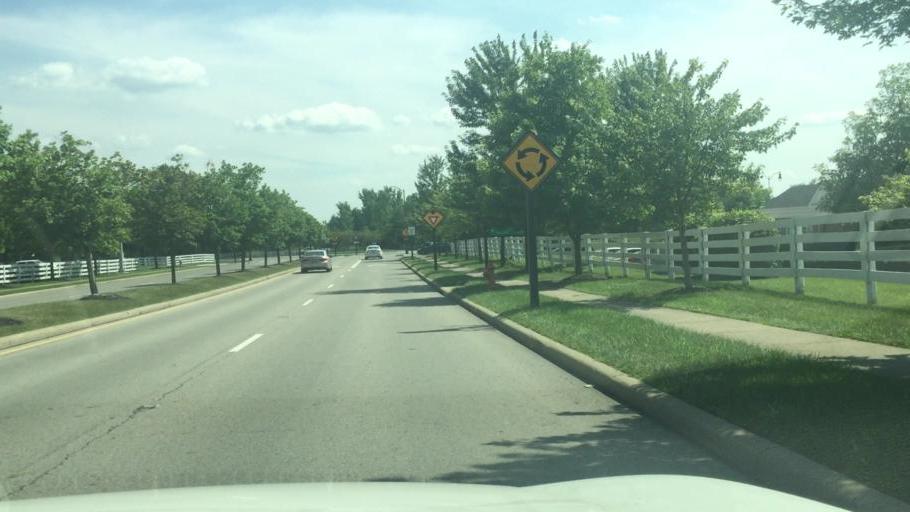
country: US
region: Ohio
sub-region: Franklin County
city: New Albany
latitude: 40.0898
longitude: -82.8247
